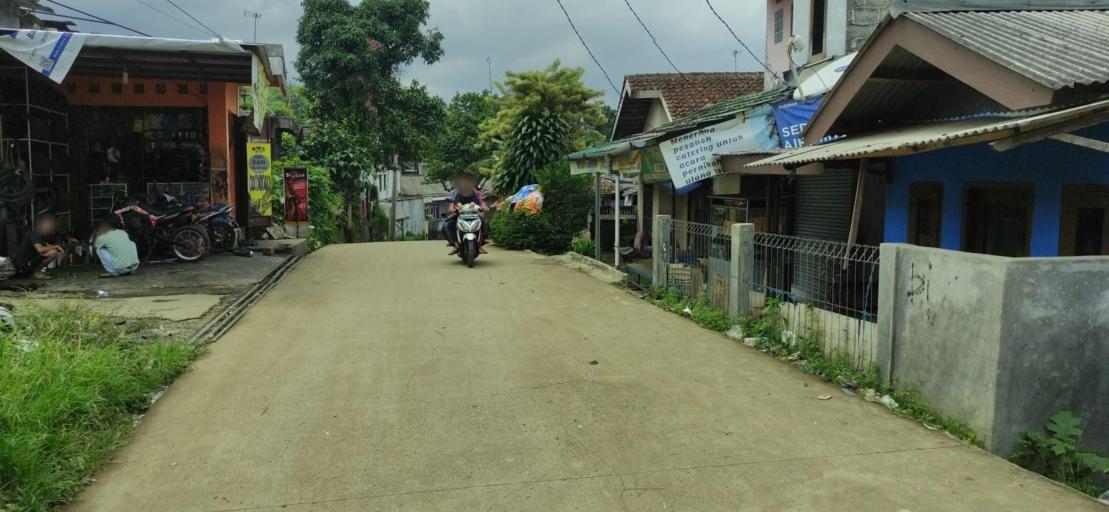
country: ID
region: West Java
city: Caringin
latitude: -6.6428
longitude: 106.8942
